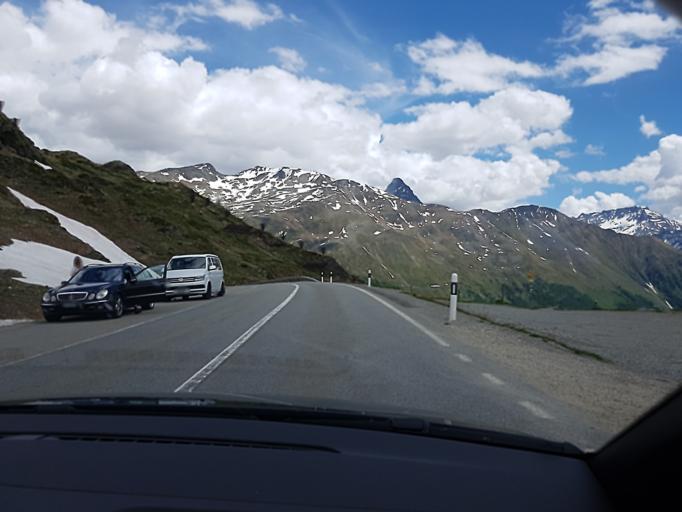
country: CH
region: Grisons
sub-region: Bernina District
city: Poschiavo
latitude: 46.4109
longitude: 10.0276
